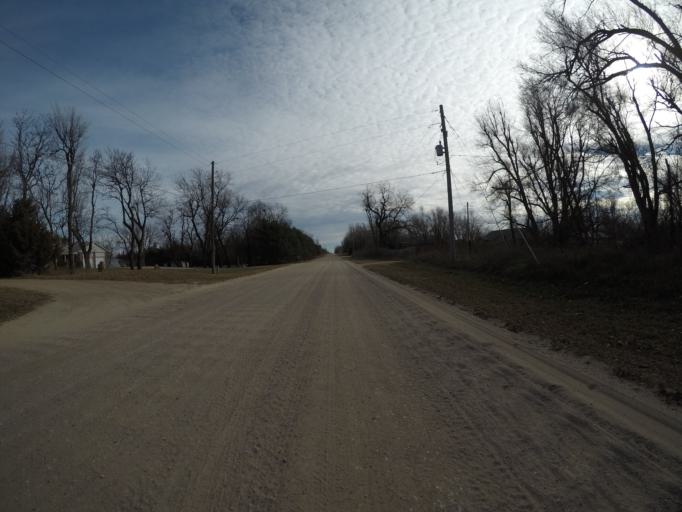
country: US
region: Kansas
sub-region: Reno County
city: Hutchinson
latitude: 38.1010
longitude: -97.8658
